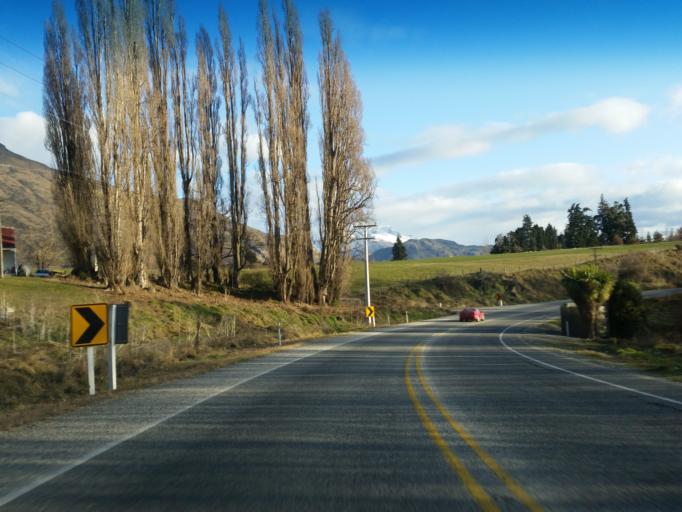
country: NZ
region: Otago
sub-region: Queenstown-Lakes District
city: Arrowtown
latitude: -44.9949
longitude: 168.8046
